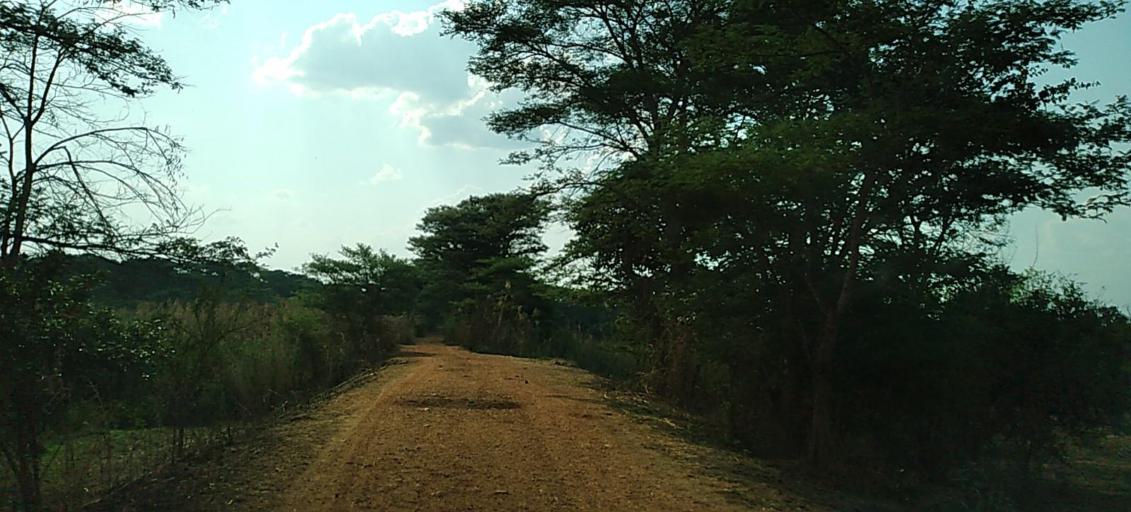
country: ZM
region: Copperbelt
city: Mpongwe
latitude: -13.4757
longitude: 28.0787
